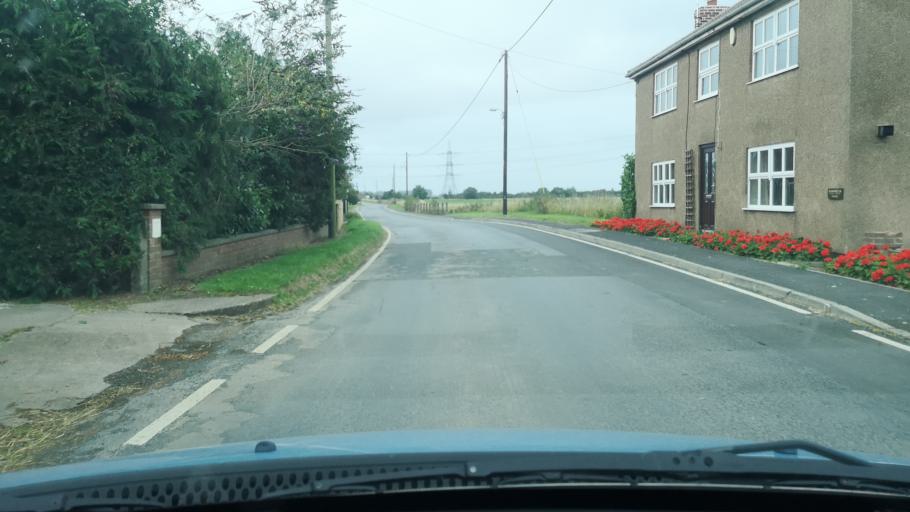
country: GB
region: England
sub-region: East Riding of Yorkshire
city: Laxton
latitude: 53.6981
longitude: -0.7378
